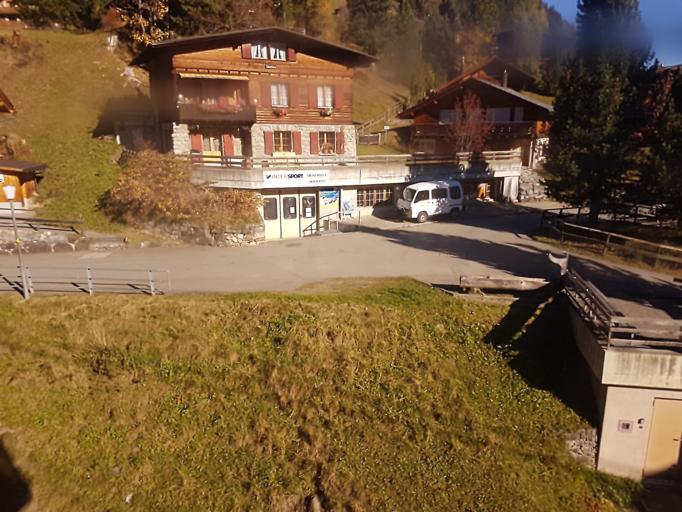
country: CH
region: Bern
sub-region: Interlaken-Oberhasli District
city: Lauterbrunnen
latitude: 46.5580
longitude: 7.8906
